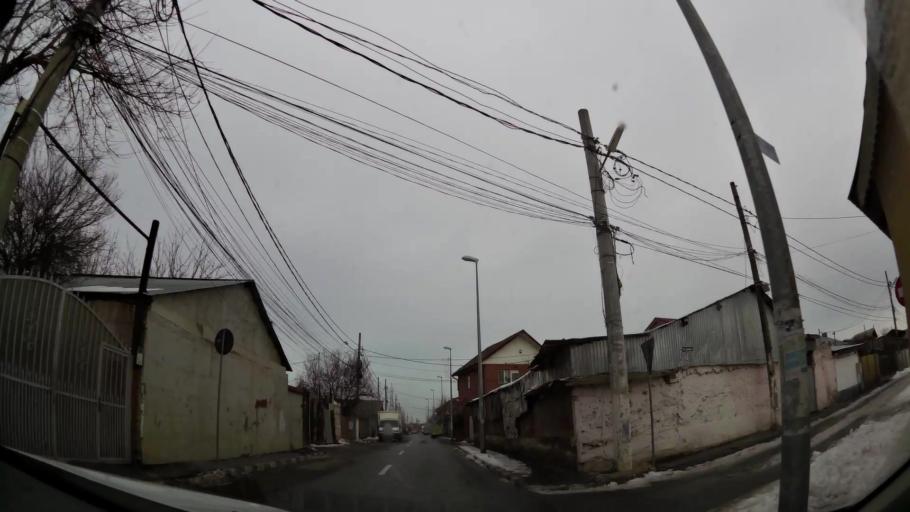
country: RO
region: Ilfov
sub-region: Comuna Pantelimon
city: Pantelimon
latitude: 44.4597
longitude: 26.2020
